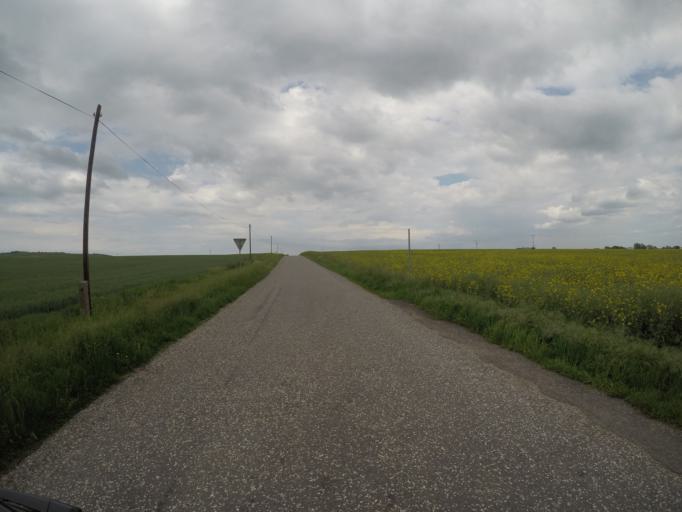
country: SK
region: Nitriansky
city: Sahy
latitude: 48.0639
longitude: 18.8567
